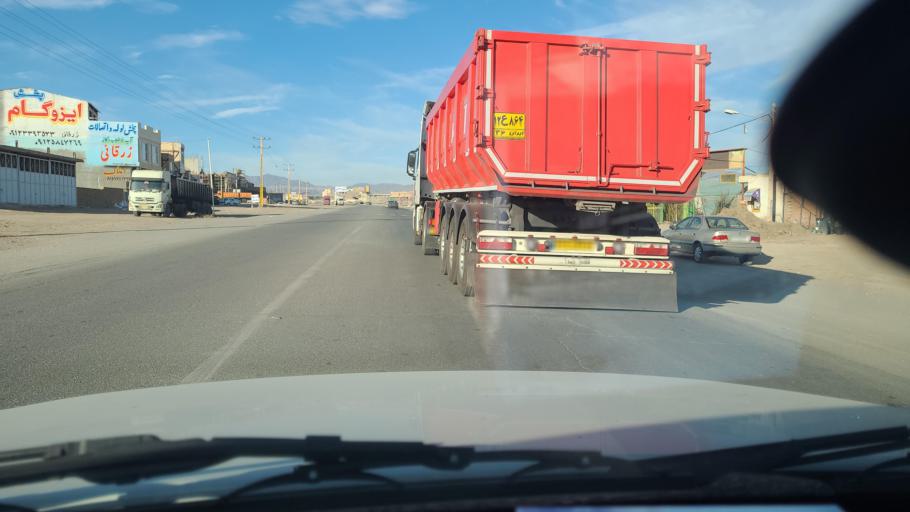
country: IR
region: Razavi Khorasan
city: Sabzevar
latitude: 36.2224
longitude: 57.6516
